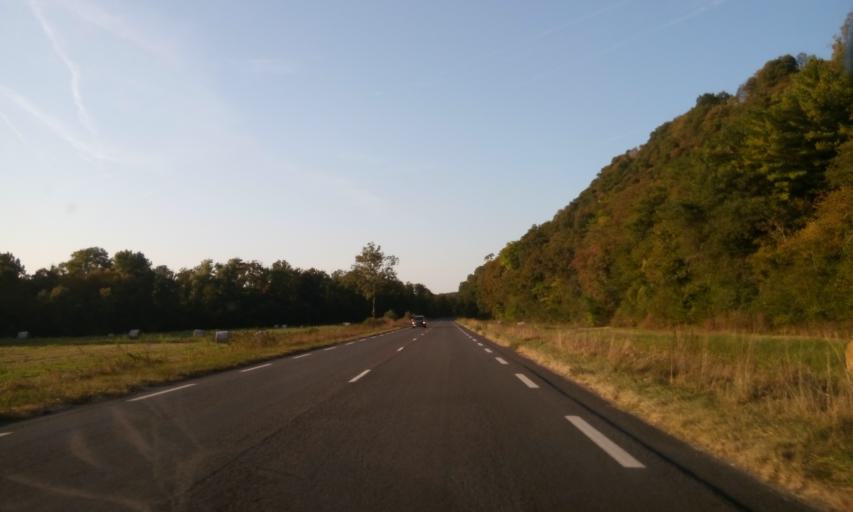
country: FR
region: Rhone-Alpes
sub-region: Departement de l'Ain
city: Neuville-sur-Ain
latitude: 46.0642
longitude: 5.3850
